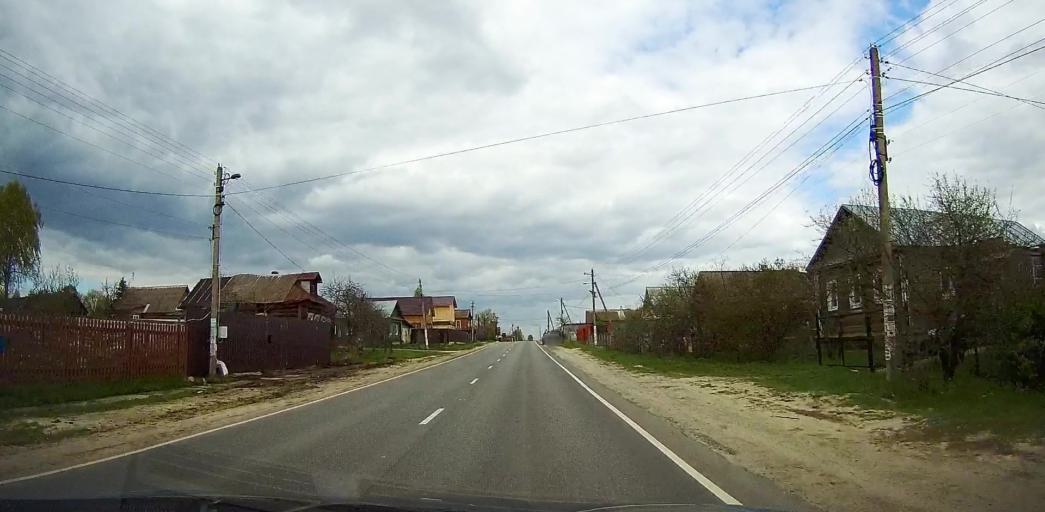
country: RU
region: Moskovskaya
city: Ashitkovo
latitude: 55.4519
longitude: 38.5938
